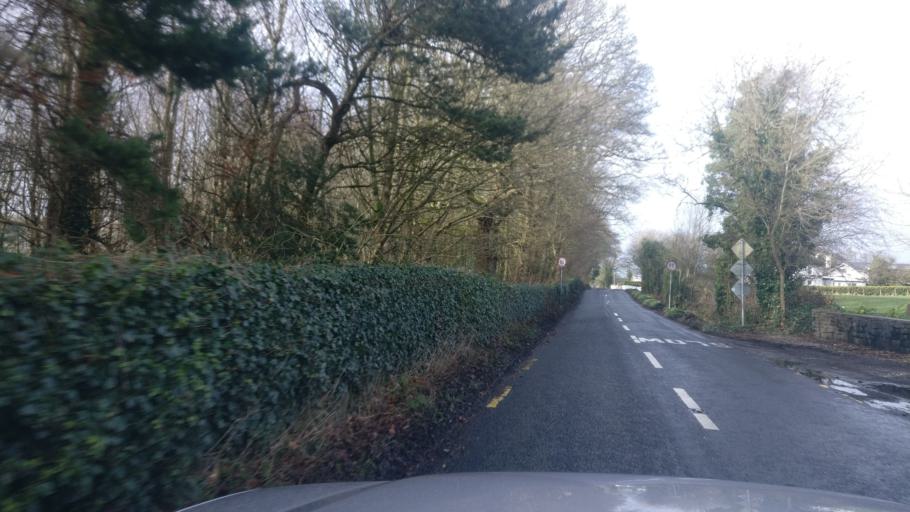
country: IE
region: Connaught
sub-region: County Galway
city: Loughrea
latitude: 53.2845
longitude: -8.5899
